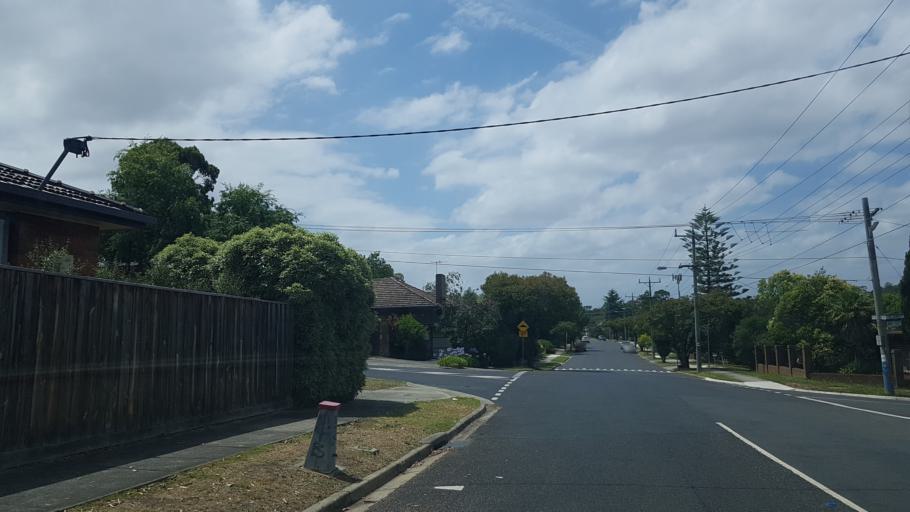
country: AU
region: Victoria
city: Rosanna
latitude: -37.7476
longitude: 145.0661
